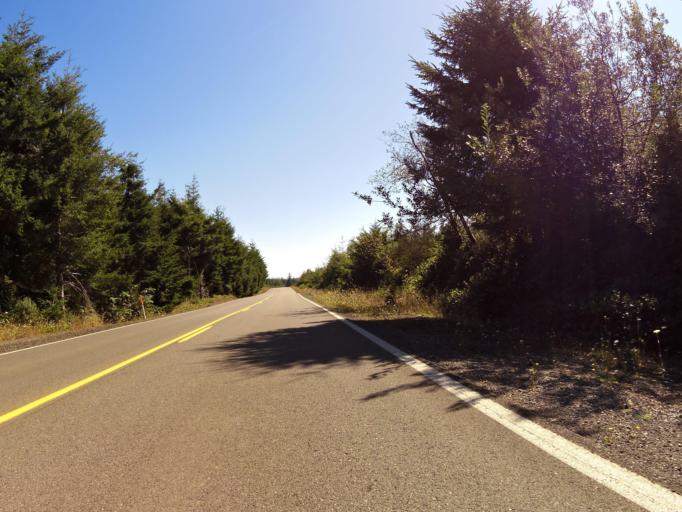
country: US
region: Oregon
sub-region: Coos County
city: Barview
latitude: 43.2607
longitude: -124.3409
